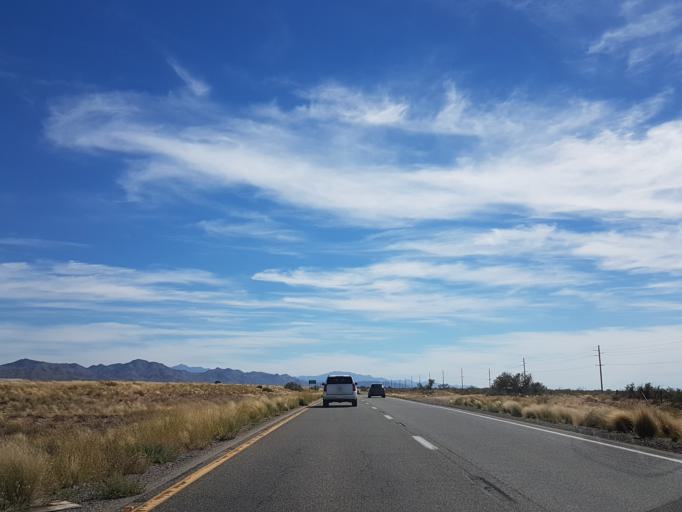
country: US
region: Arizona
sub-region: Mohave County
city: Golden Valley
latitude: 35.3805
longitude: -114.2478
